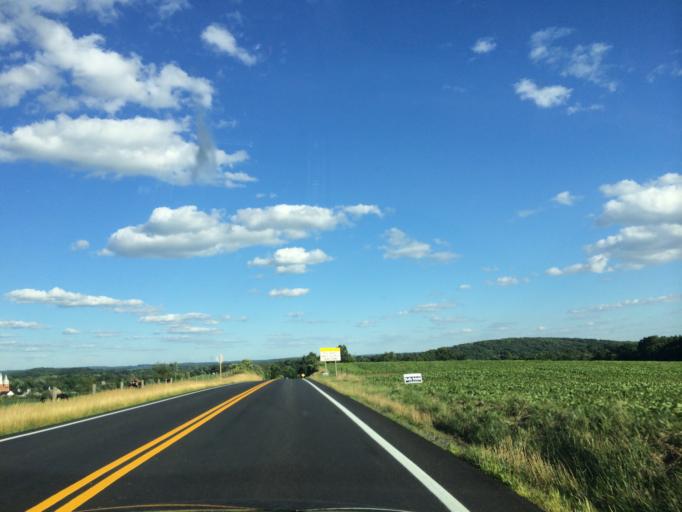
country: US
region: Maryland
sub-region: Frederick County
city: Linganore
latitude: 39.4909
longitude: -77.2513
